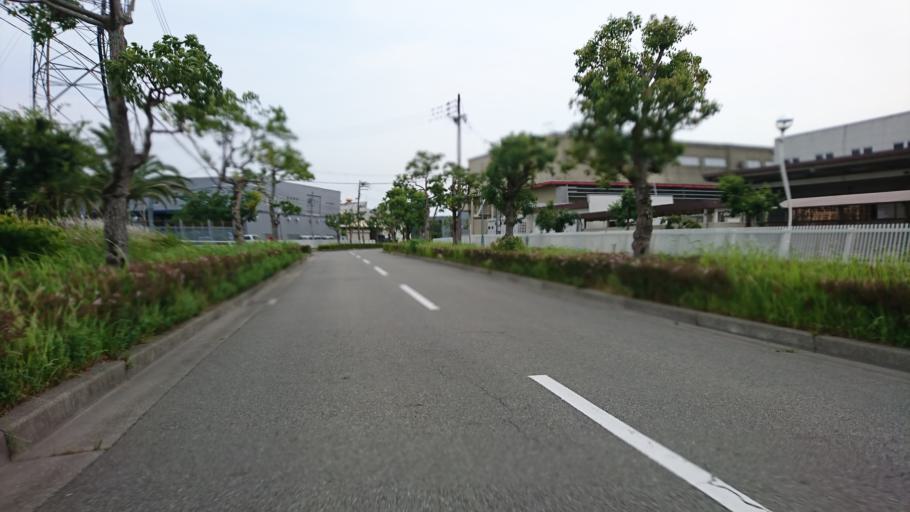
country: JP
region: Hyogo
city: Kakogawacho-honmachi
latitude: 34.7375
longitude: 134.8855
